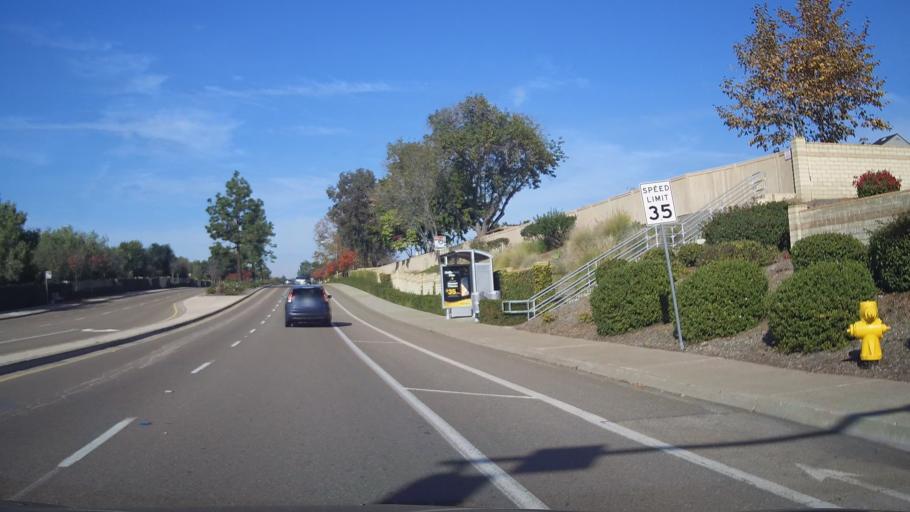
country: US
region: California
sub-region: San Diego County
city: La Mesa
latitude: 32.8102
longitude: -117.1060
